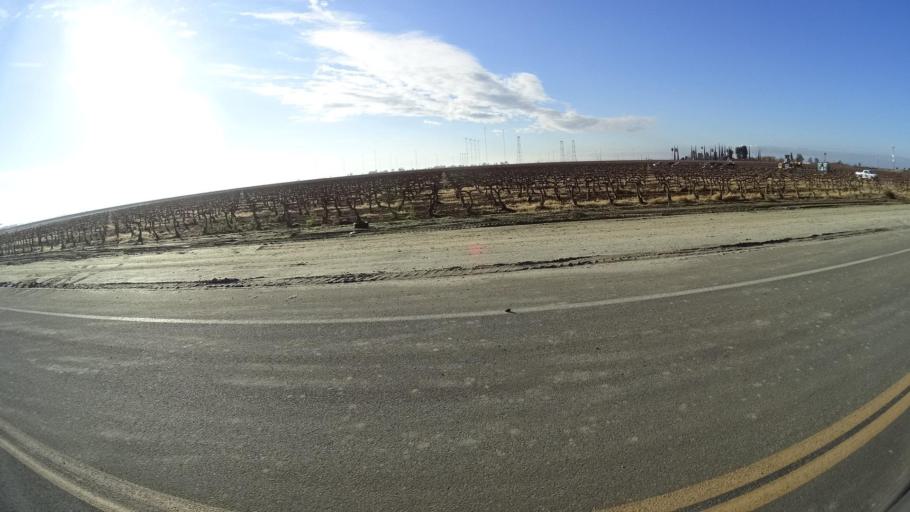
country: US
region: California
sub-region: Kern County
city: Delano
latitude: 35.7687
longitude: -119.2819
